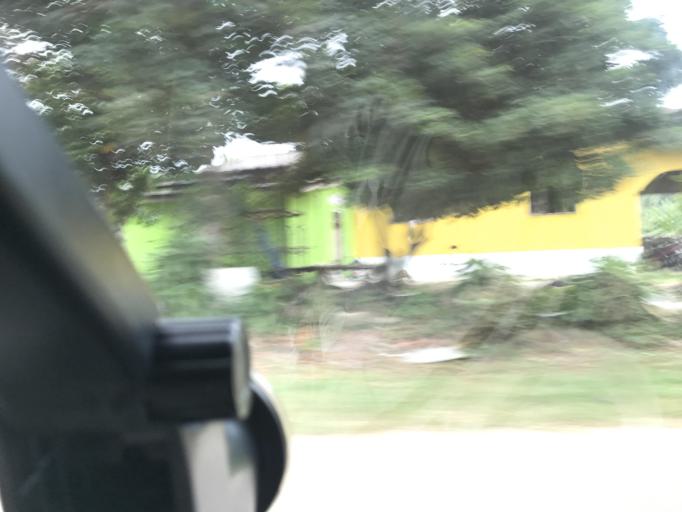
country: MY
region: Kelantan
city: Tumpat
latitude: 6.1738
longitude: 102.2071
